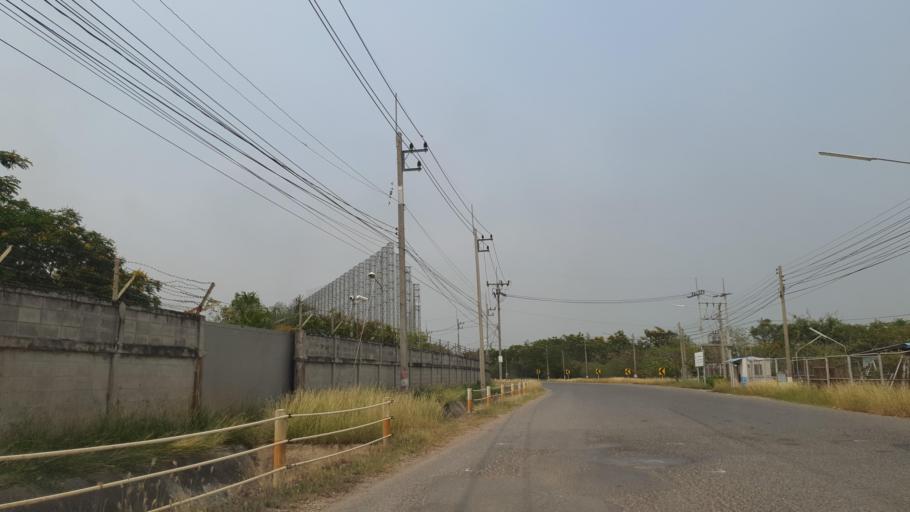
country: TH
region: Chachoengsao
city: Bang Pakong
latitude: 13.5006
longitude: 101.0334
